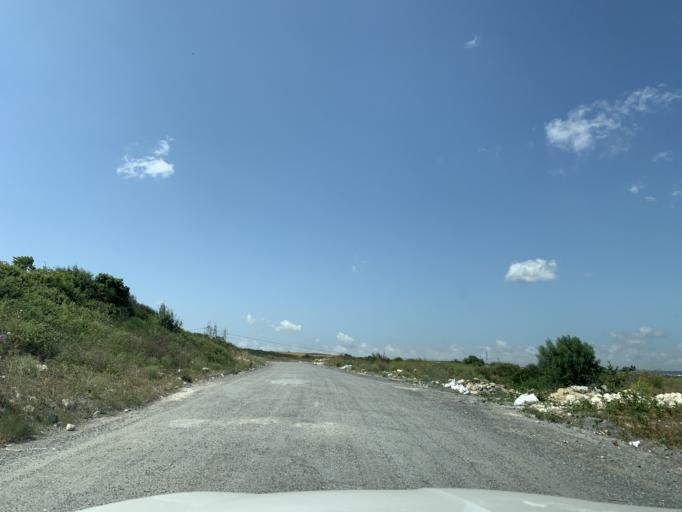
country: TR
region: Istanbul
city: Esenyurt
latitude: 41.0834
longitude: 28.6936
